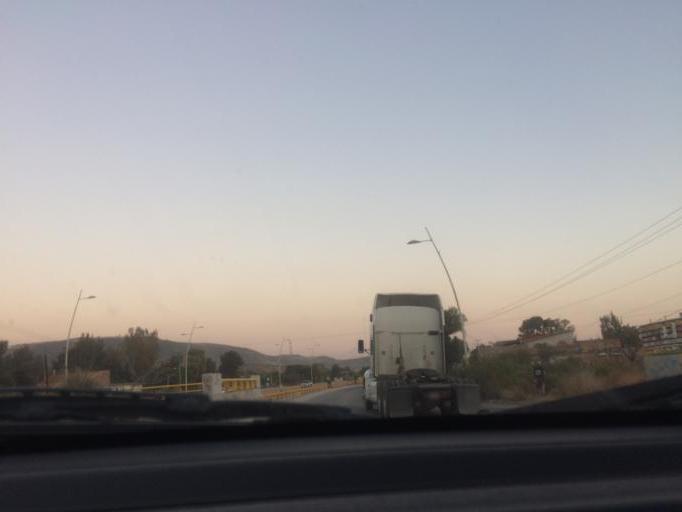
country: MX
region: Guanajuato
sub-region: Leon
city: Fraccionamiento Paraiso Real
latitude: 21.1293
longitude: -101.6017
